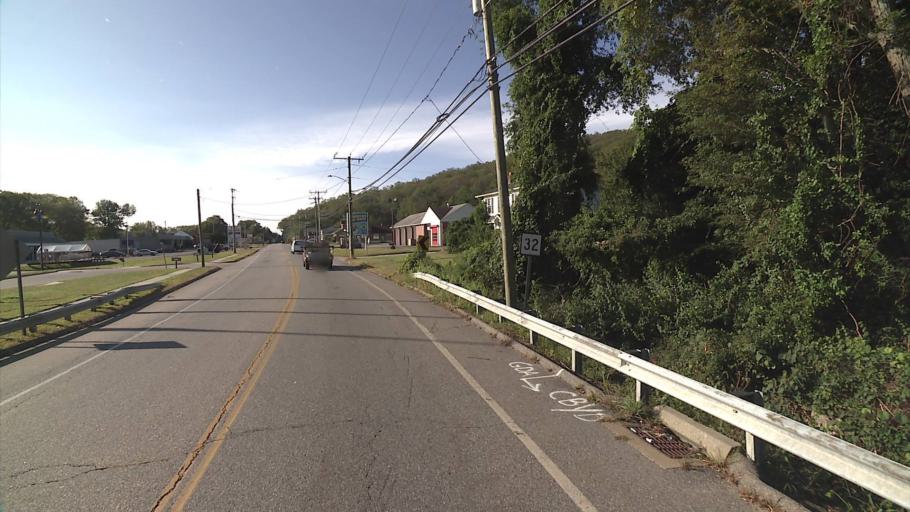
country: US
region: Connecticut
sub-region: New London County
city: Uncasville
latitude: 41.4514
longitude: -72.1074
